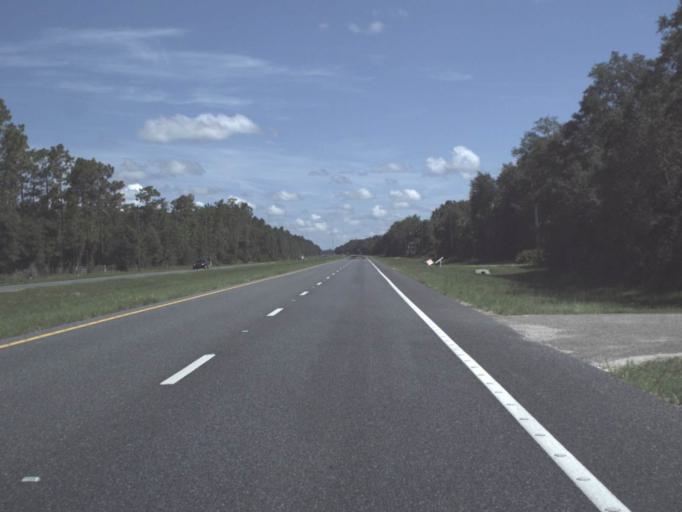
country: US
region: Florida
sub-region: Levy County
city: Inglis
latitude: 29.1259
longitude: -82.6367
